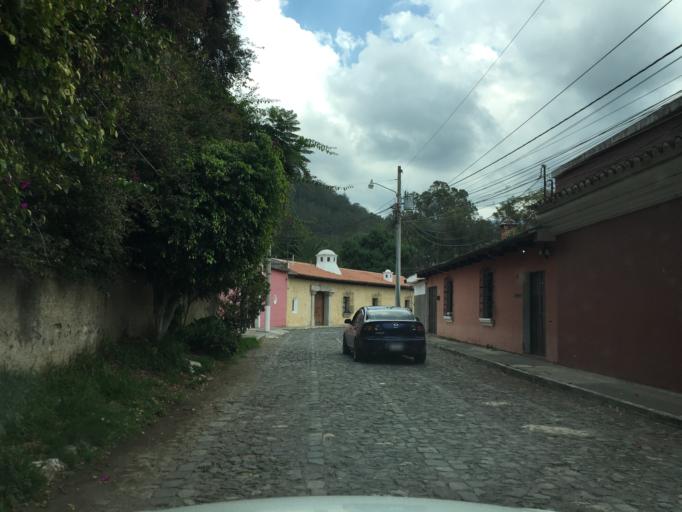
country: GT
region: Sacatepequez
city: Antigua Guatemala
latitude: 14.5622
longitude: -90.7278
